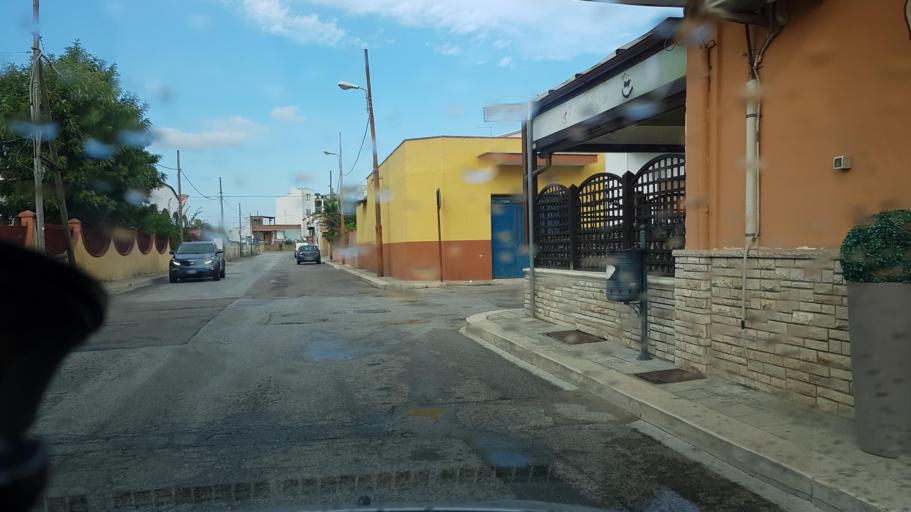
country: IT
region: Apulia
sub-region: Provincia di Brindisi
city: Torre Santa Susanna
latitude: 40.4683
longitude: 17.7353
